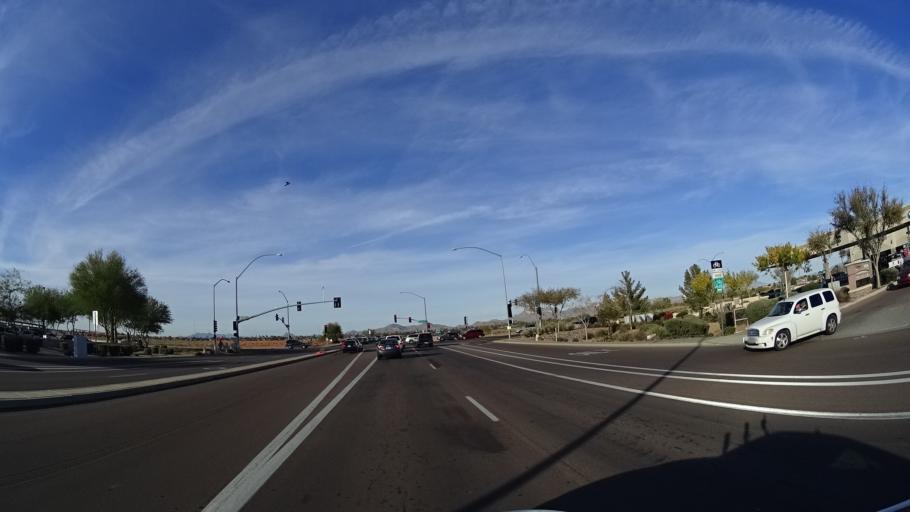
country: US
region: Arizona
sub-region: Pinal County
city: Apache Junction
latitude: 33.3783
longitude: -111.6362
